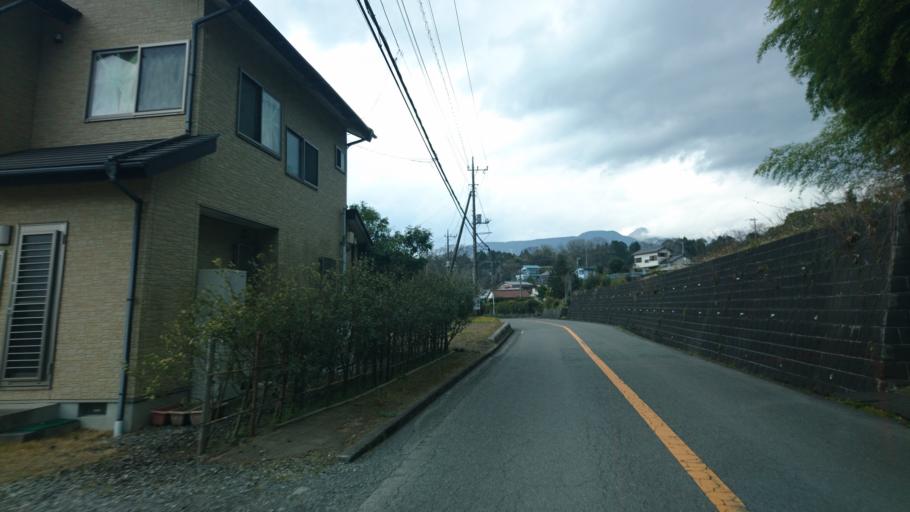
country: JP
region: Shizuoka
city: Fujinomiya
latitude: 35.2691
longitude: 138.5928
